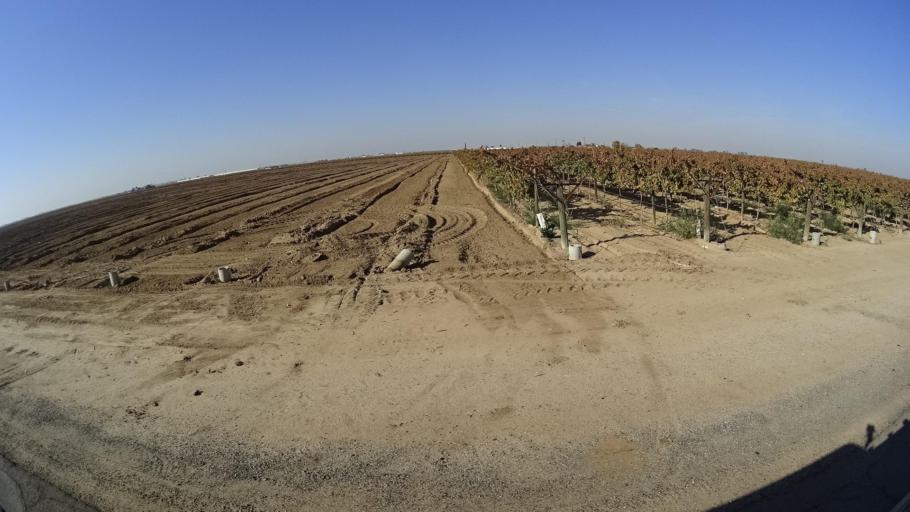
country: US
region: California
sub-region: Kern County
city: Delano
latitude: 35.7387
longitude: -119.2052
